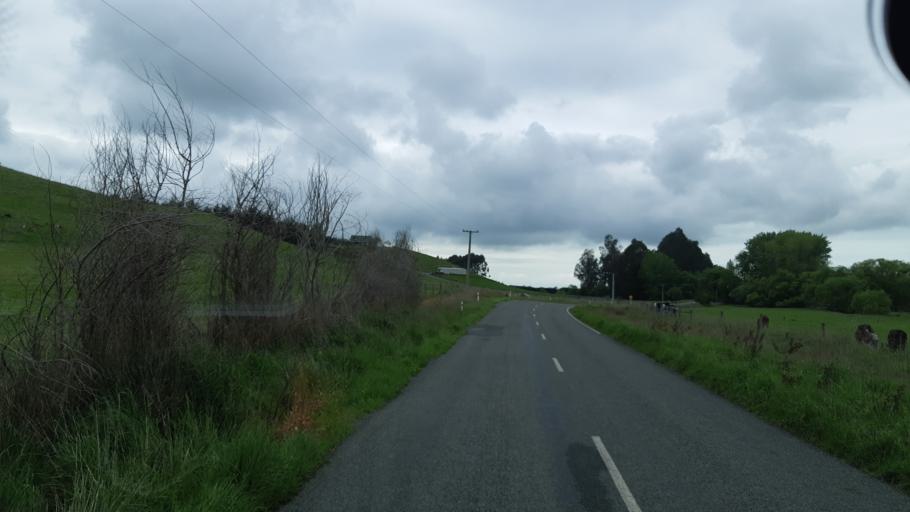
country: NZ
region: Canterbury
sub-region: Timaru District
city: Pleasant Point
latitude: -44.3010
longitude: 171.1608
